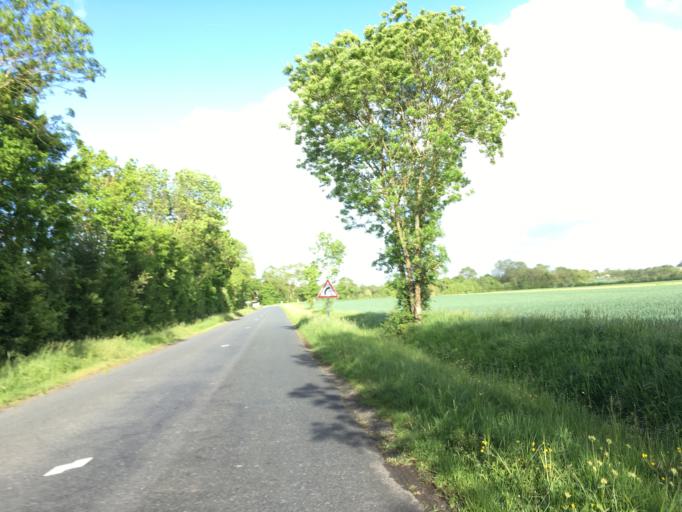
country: FR
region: Poitou-Charentes
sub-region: Departement de la Charente-Maritime
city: Verines
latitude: 46.1695
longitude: -0.8793
